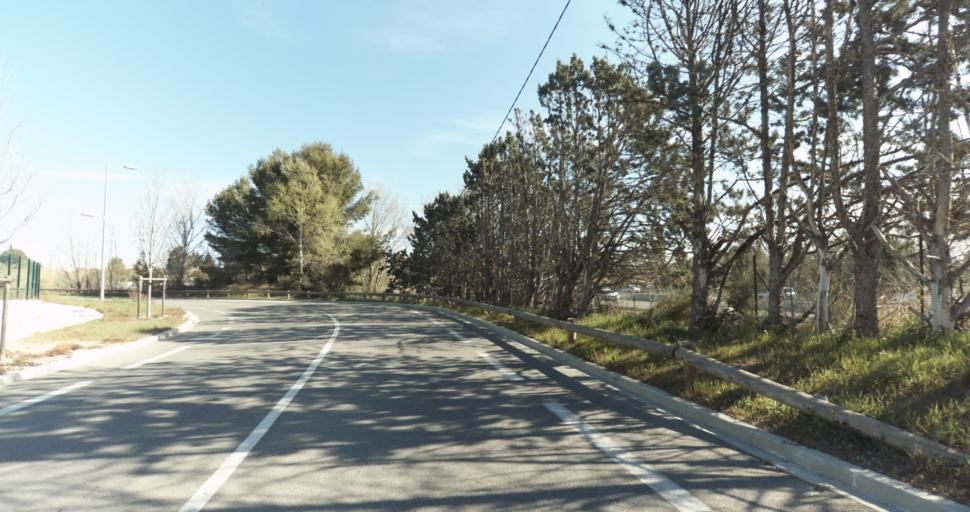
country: FR
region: Provence-Alpes-Cote d'Azur
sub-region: Departement des Bouches-du-Rhone
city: Aix-en-Provence
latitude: 43.5150
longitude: 5.4271
